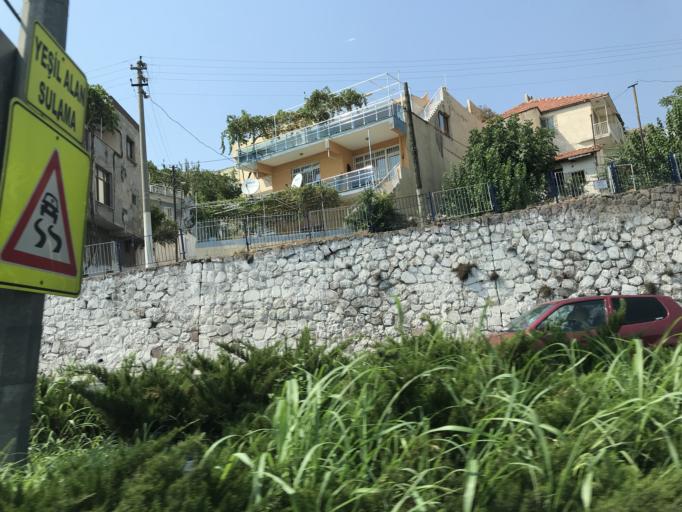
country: TR
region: Izmir
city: Izmir
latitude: 38.3953
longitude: 27.1368
